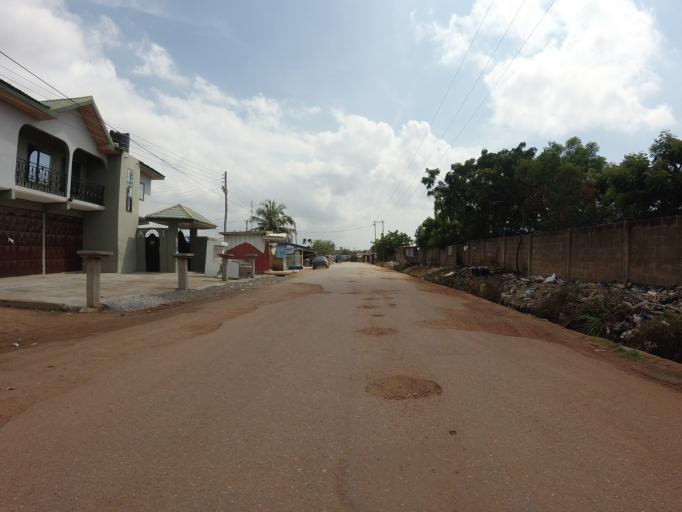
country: GH
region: Greater Accra
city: Nungua
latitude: 5.6087
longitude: -0.0846
